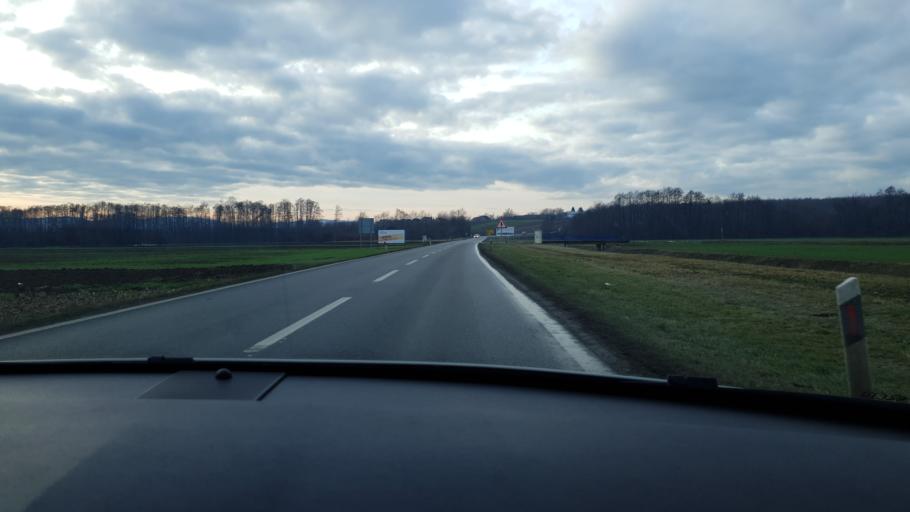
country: HR
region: Pozesko-Slavonska
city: Jaksic
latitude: 45.3556
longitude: 17.7543
